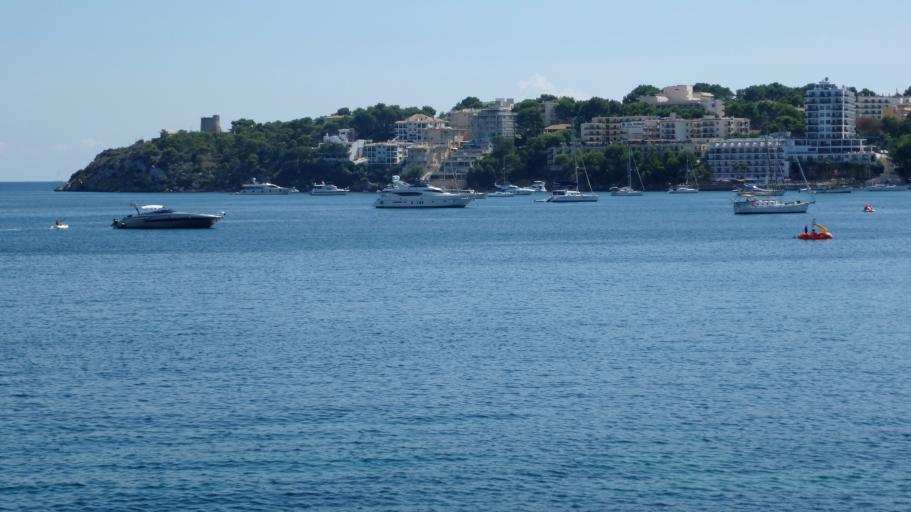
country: ES
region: Balearic Islands
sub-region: Illes Balears
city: Magaluf
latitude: 39.5214
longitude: 2.5387
